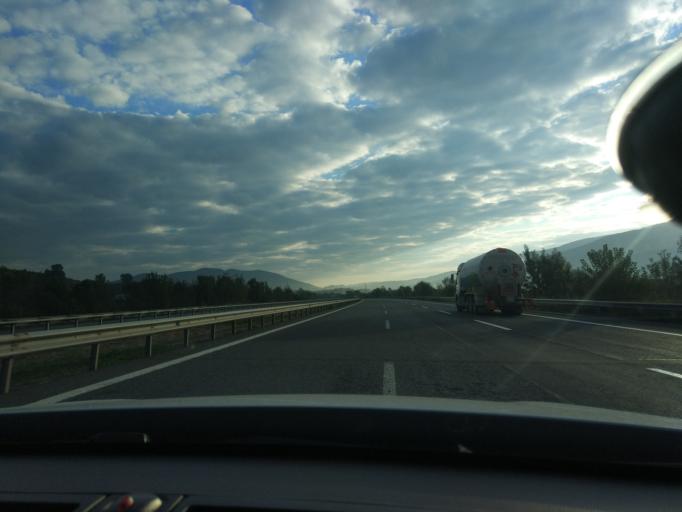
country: TR
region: Sakarya
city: Karadere
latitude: 40.7874
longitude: 30.8255
